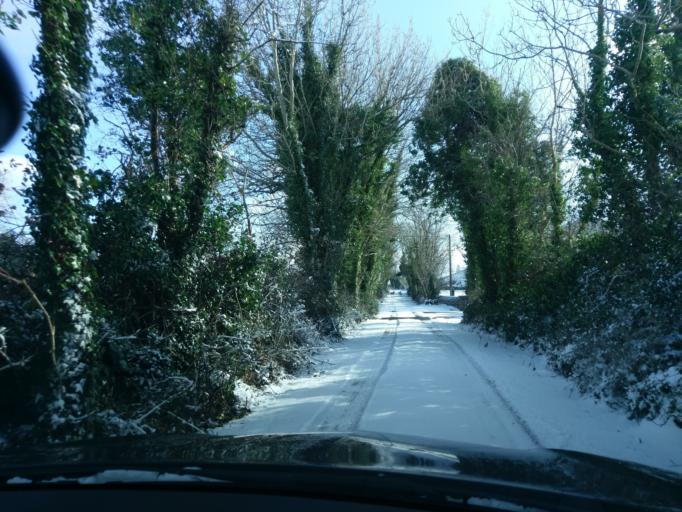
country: IE
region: Connaught
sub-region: County Galway
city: Athenry
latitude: 53.2083
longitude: -8.7694
